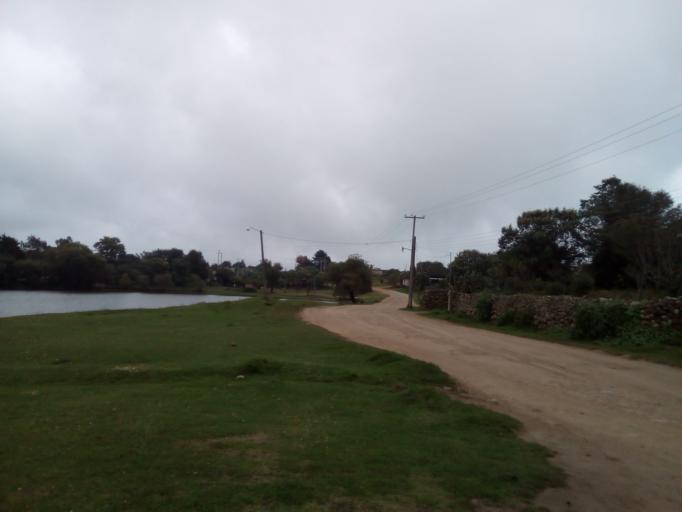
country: MX
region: San Luis Potosi
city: Tierranueva
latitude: 21.5040
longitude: -100.4396
